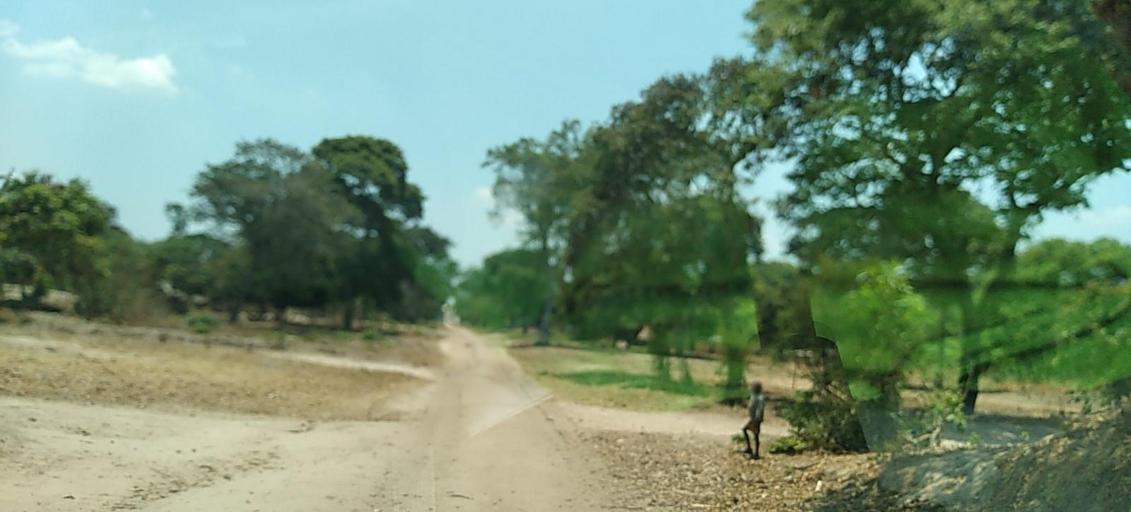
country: CD
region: Katanga
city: Kolwezi
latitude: -11.3712
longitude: 25.2131
